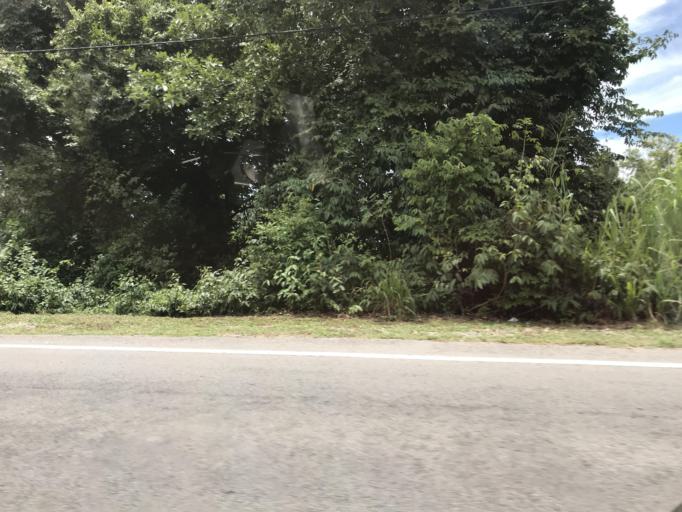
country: MY
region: Kelantan
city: Tumpat
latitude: 6.1747
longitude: 102.2002
